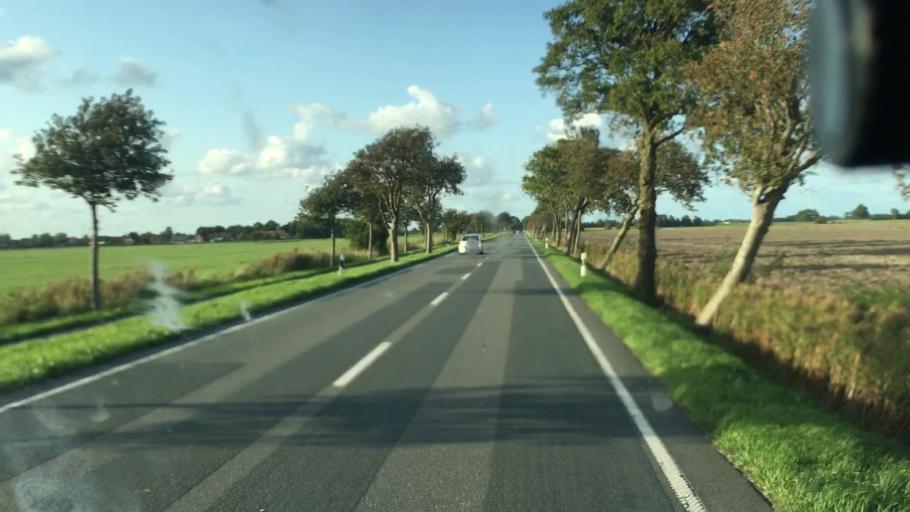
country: DE
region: Lower Saxony
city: Wittmund
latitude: 53.6464
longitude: 7.7901
